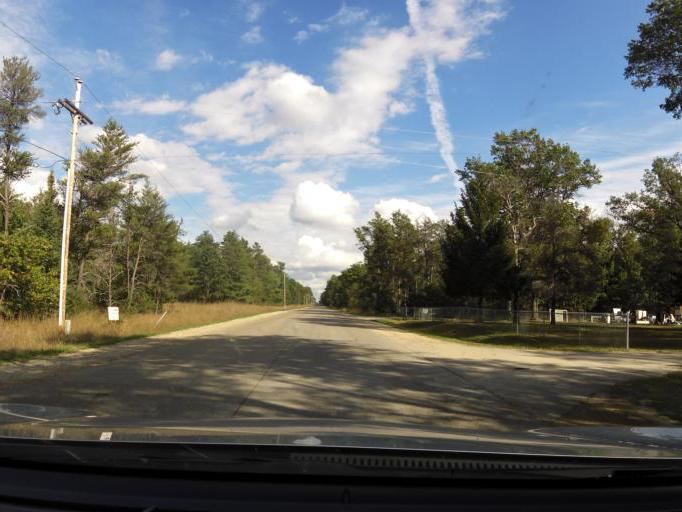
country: US
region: Michigan
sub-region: Roscommon County
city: Roscommon
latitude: 44.5257
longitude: -84.5863
